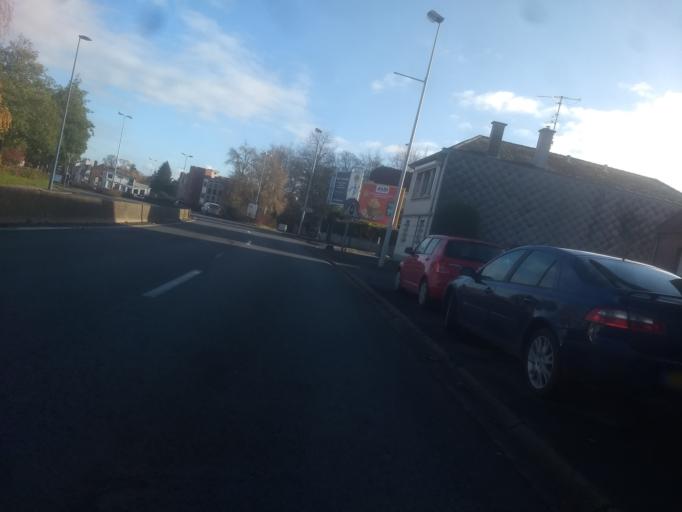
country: FR
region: Nord-Pas-de-Calais
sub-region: Departement du Pas-de-Calais
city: Sainte-Catherine
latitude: 50.2972
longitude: 2.7534
